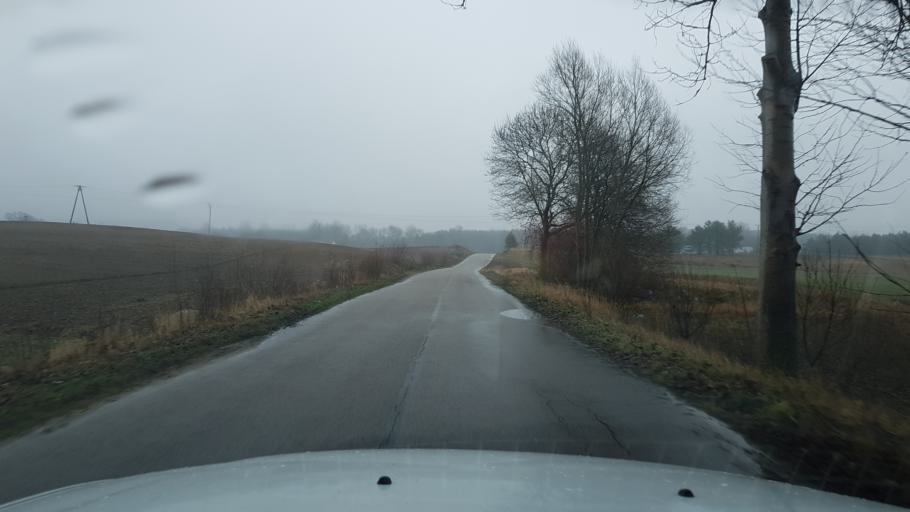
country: PL
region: West Pomeranian Voivodeship
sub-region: Powiat drawski
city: Czaplinek
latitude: 53.5792
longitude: 16.2401
